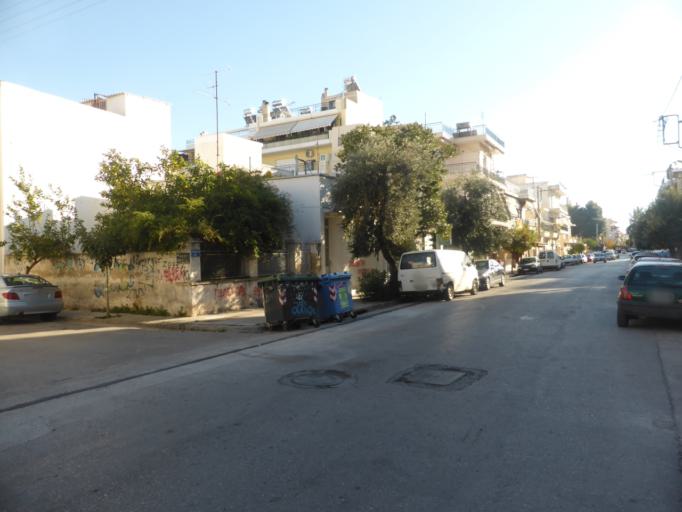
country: GR
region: Attica
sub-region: Nomarchia Athinas
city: Peristeri
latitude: 38.0147
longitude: 23.6984
